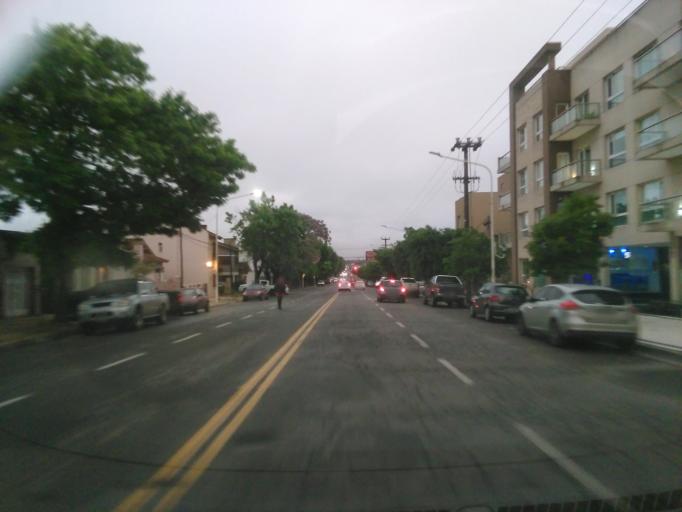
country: AR
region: Buenos Aires
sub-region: Partido de Tandil
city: Tandil
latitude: -37.3303
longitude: -59.1445
